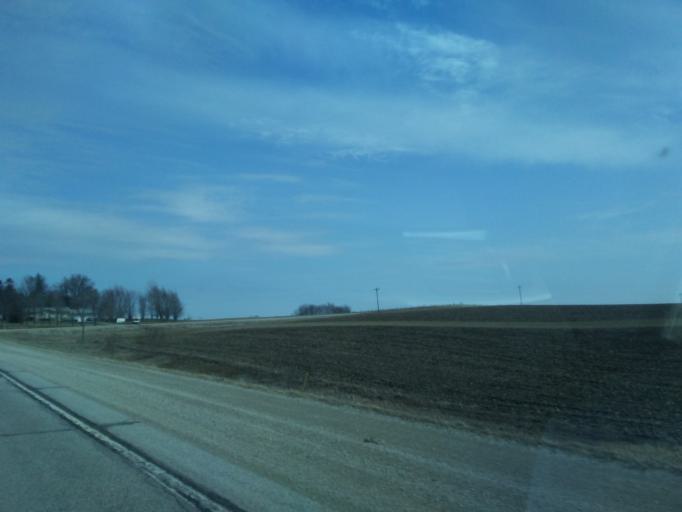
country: US
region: Iowa
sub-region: Allamakee County
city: Waukon
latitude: 43.2405
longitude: -91.5096
